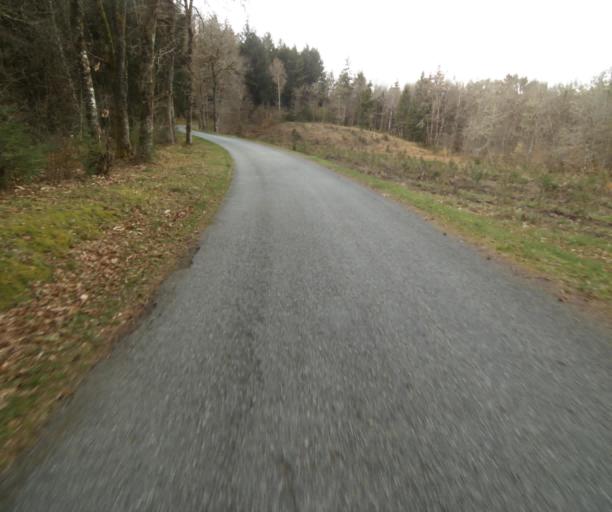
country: FR
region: Limousin
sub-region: Departement de la Correze
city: Correze
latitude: 45.2918
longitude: 1.9640
